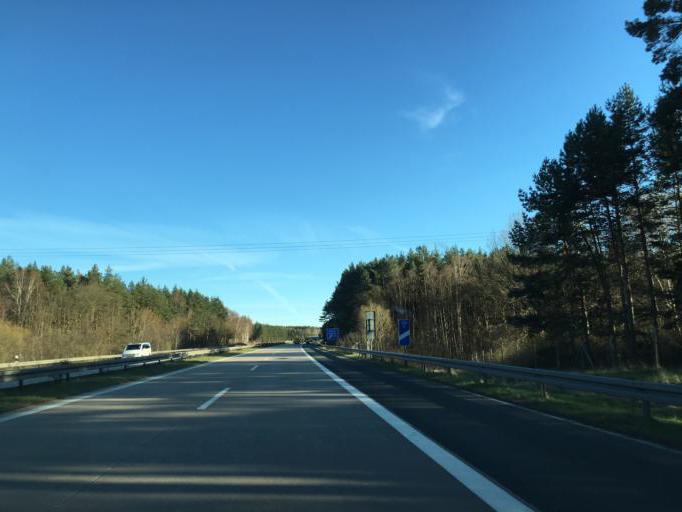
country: DE
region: Mecklenburg-Vorpommern
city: Lalendorf
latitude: 53.7806
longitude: 12.3155
